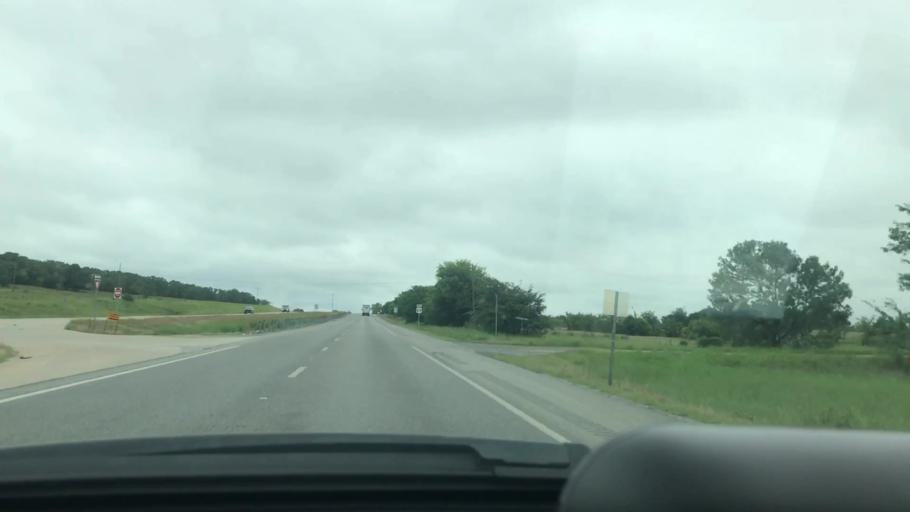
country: US
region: Oklahoma
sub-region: Coal County
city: Coalgate
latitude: 34.6657
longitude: -95.9379
